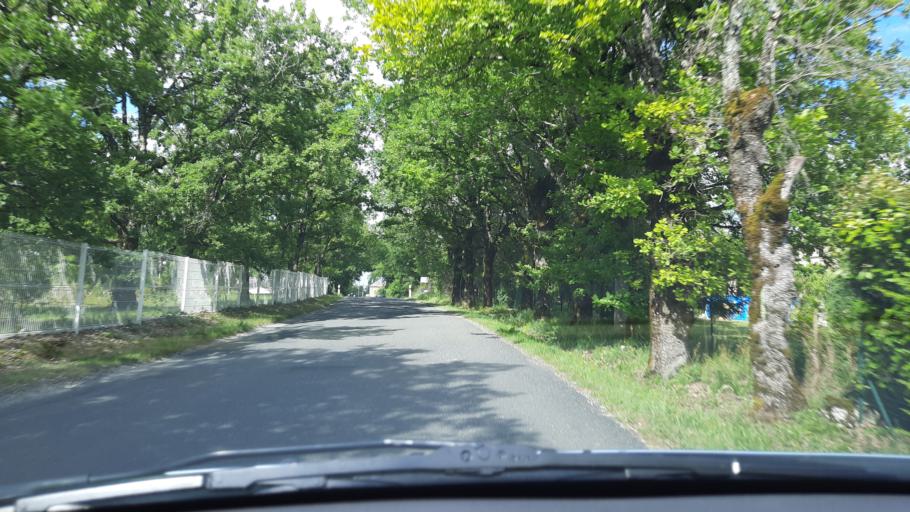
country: FR
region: Midi-Pyrenees
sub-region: Departement du Lot
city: Lalbenque
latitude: 44.2971
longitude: 1.4660
